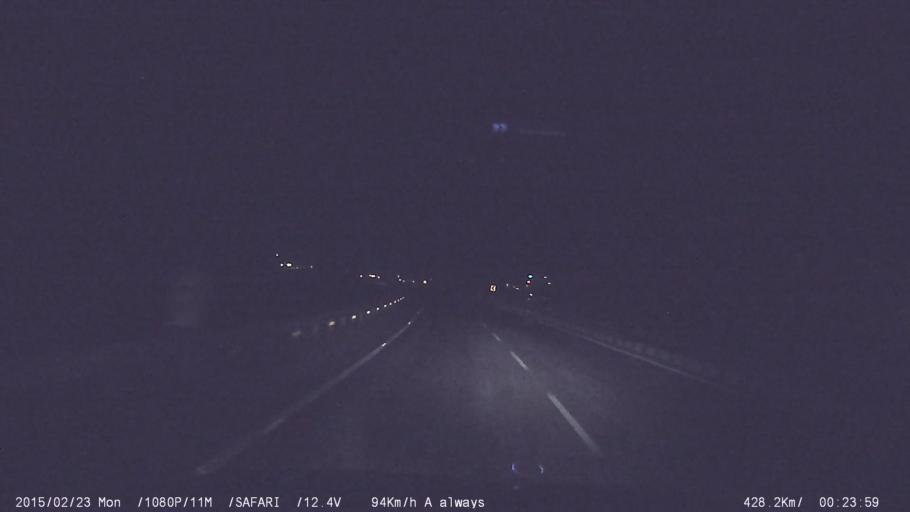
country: IN
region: Tamil Nadu
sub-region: Dharmapuri
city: Mallapuram
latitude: 11.9305
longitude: 78.0649
